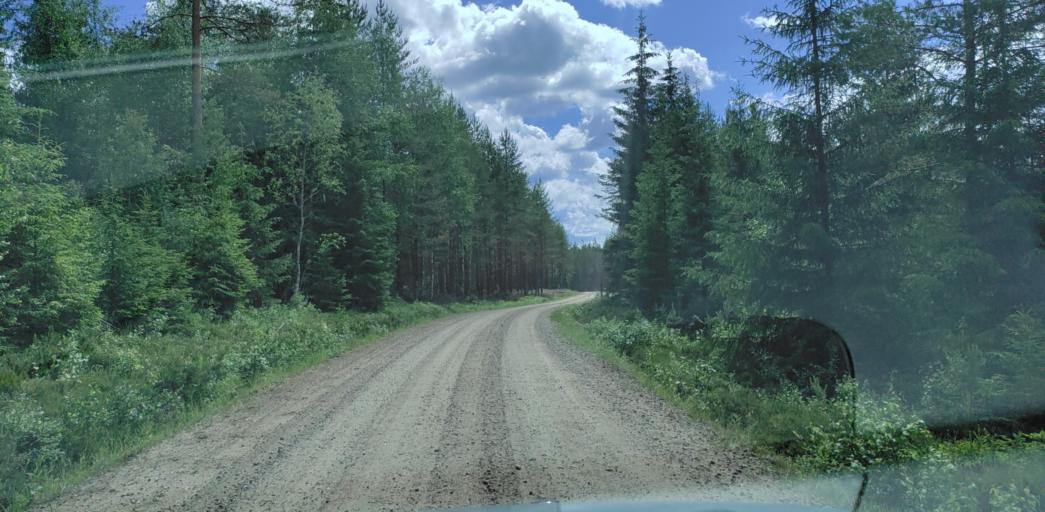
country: SE
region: Vaermland
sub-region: Hagfors Kommun
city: Ekshaerad
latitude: 60.0677
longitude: 13.2905
